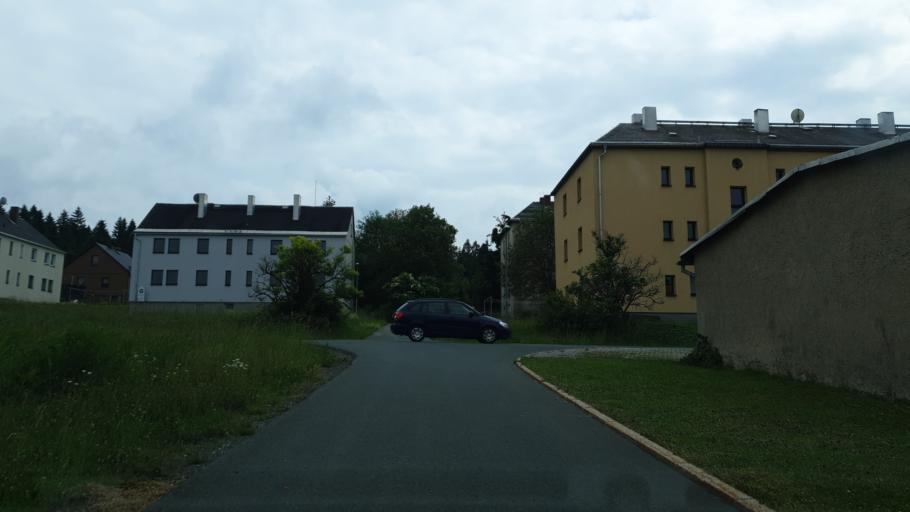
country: DE
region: Saxony
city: Tannenbergsthal
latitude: 50.4139
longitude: 12.4444
